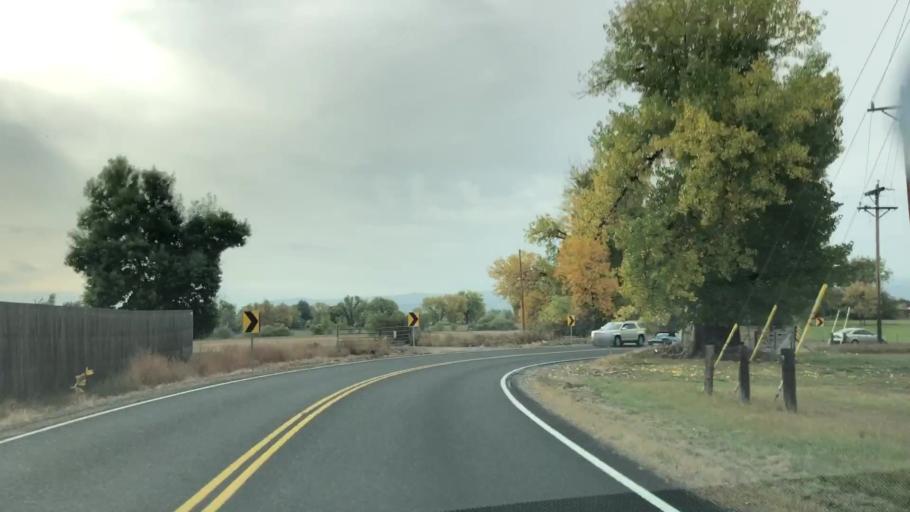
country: US
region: Colorado
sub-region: Larimer County
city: Loveland
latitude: 40.4678
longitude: -105.0577
